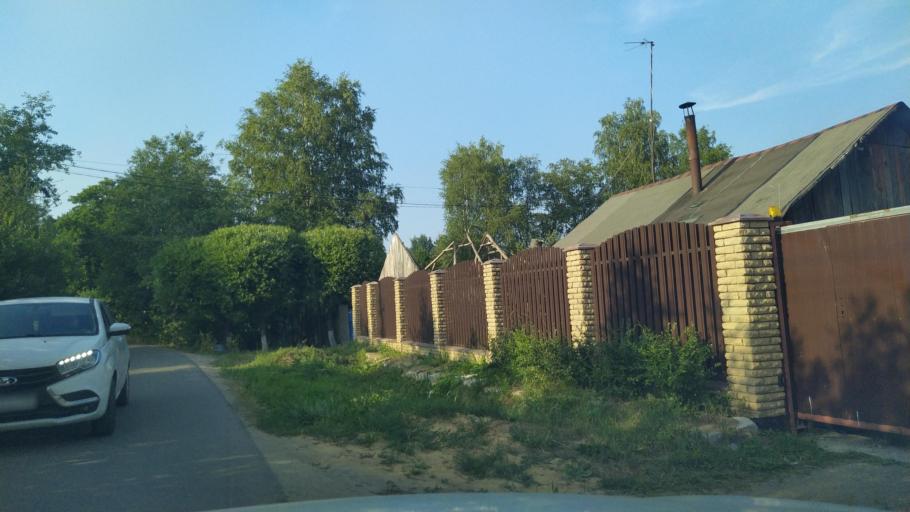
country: RU
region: Leningrad
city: Koltushi
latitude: 59.8933
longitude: 30.7328
